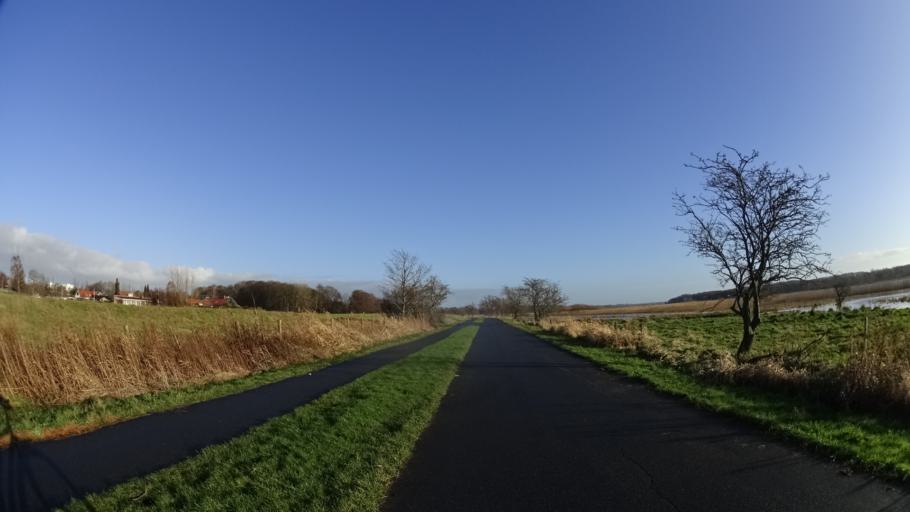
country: DK
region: Central Jutland
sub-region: Arhus Kommune
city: Stavtrup
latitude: 56.1445
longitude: 10.1364
